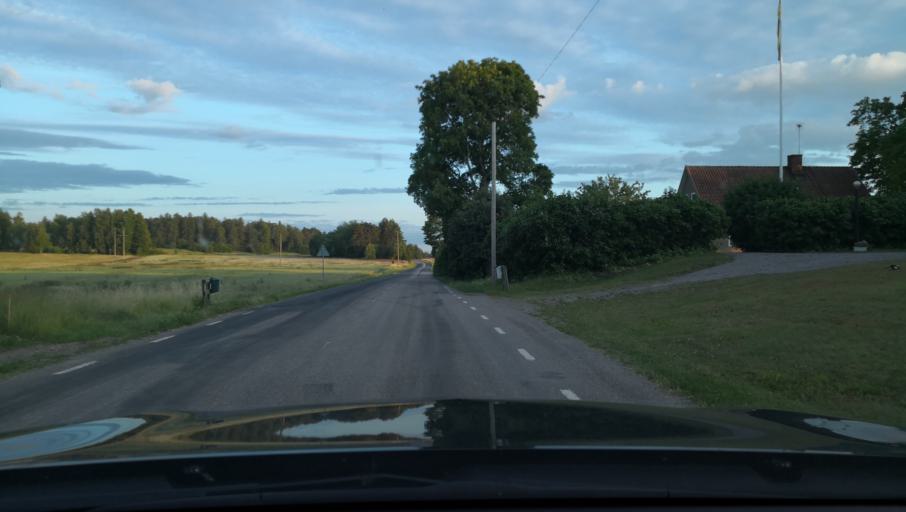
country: SE
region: Uppsala
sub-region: Uppsala Kommun
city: Vattholma
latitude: 60.0207
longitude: 17.7213
